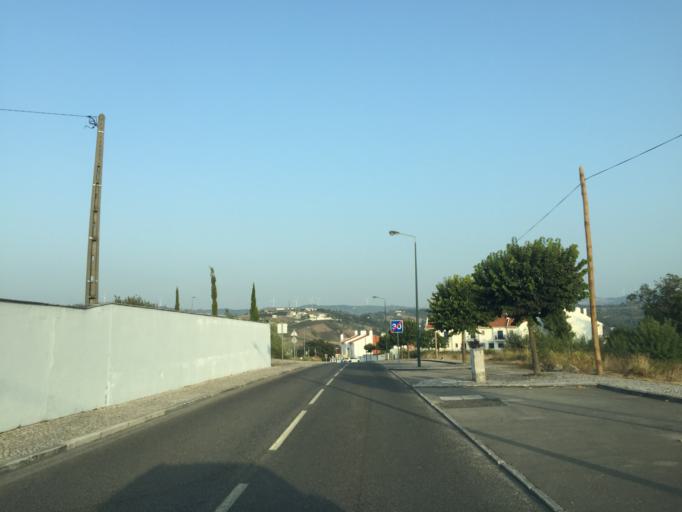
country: PT
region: Leiria
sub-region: Batalha
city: Batalha
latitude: 39.6607
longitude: -8.8311
